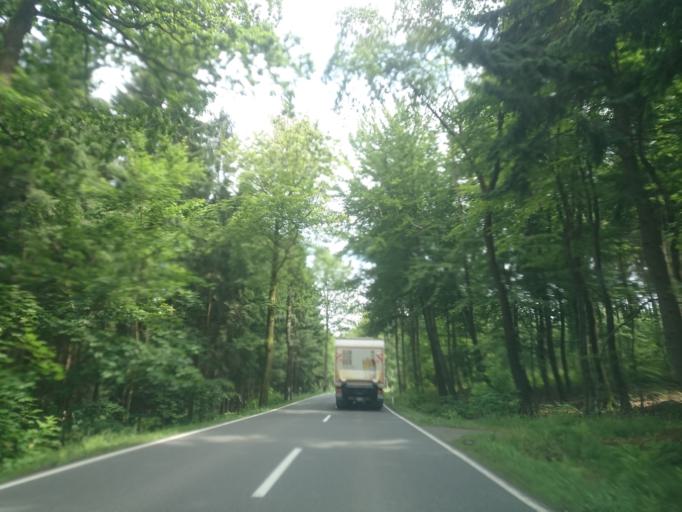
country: DE
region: Saxony
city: Augustusburg
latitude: 50.7895
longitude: 13.1133
